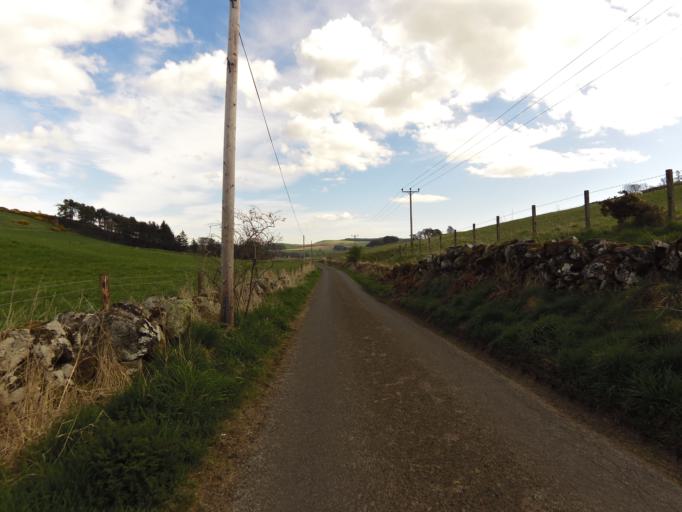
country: GB
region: Scotland
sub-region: Fife
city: Newburgh
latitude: 56.3360
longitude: -3.2474
